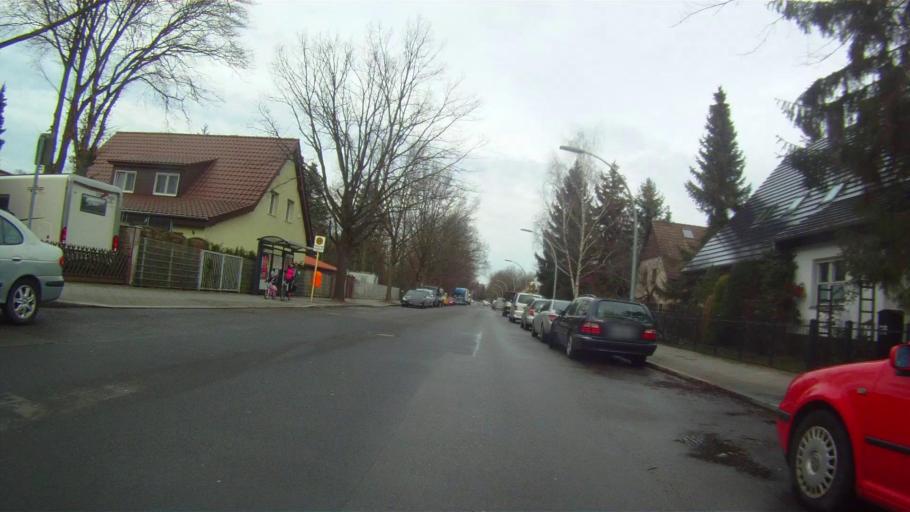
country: DE
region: Berlin
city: Lichtenrade
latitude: 52.3904
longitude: 13.4123
